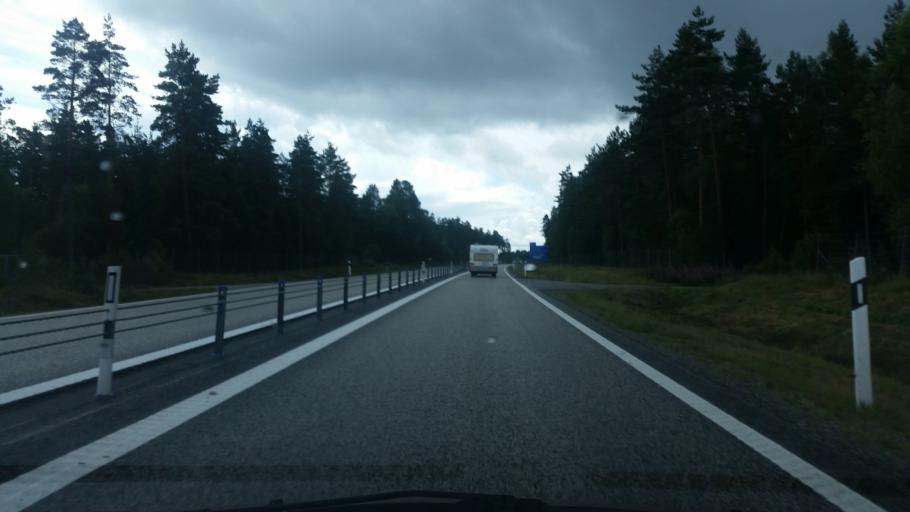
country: SE
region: Joenkoeping
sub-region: Gislaveds Kommun
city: Gislaved
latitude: 57.3316
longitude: 13.5476
